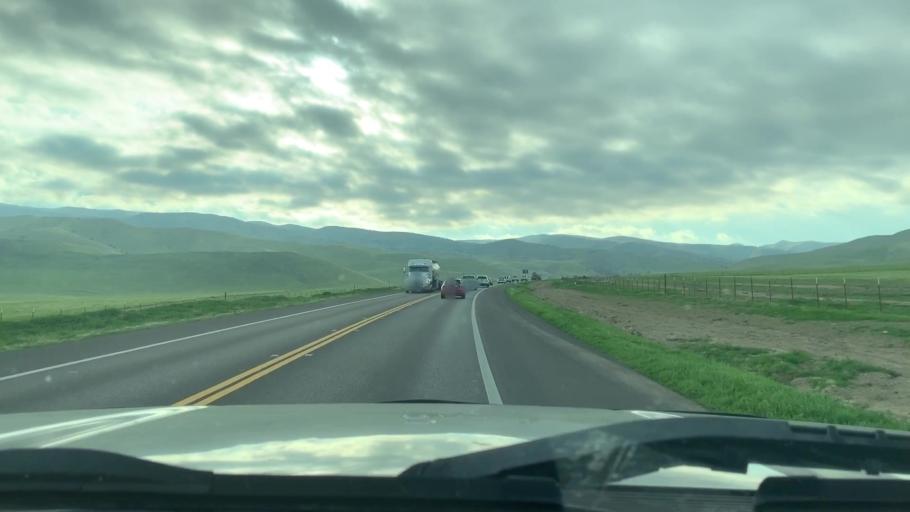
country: US
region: California
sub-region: Kings County
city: Avenal
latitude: 35.7855
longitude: -120.1162
